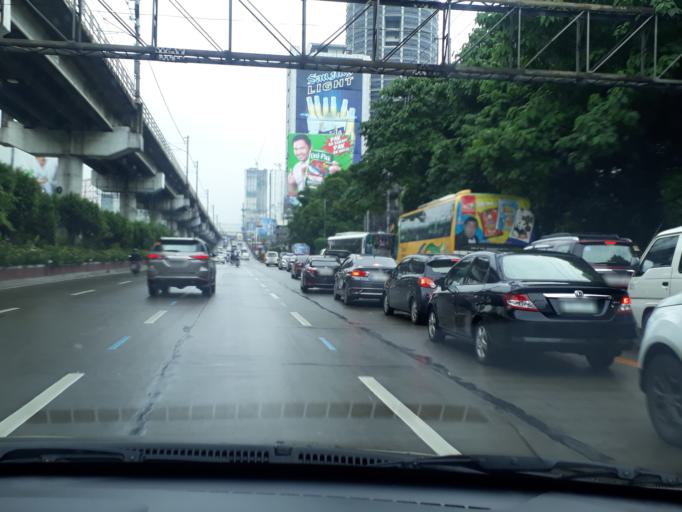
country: PH
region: Calabarzon
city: Bagong Pagasa
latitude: 14.6474
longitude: 121.0353
